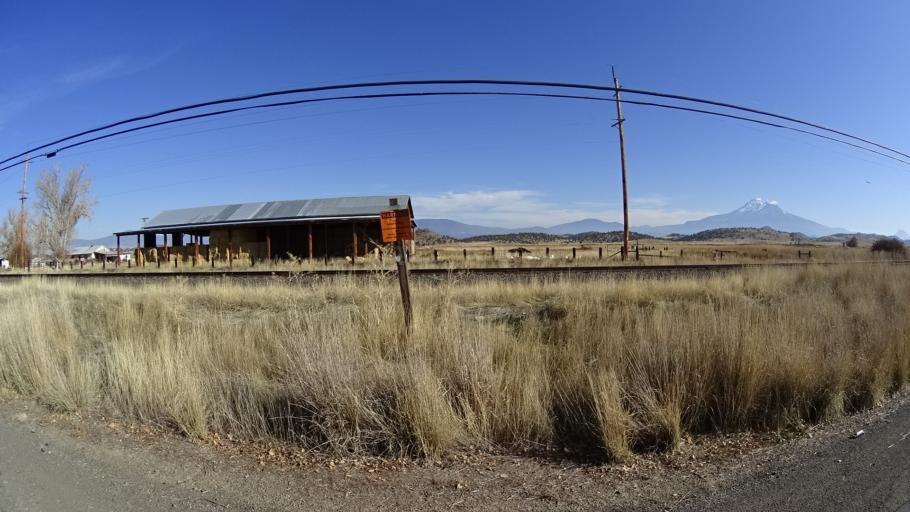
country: US
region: California
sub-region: Siskiyou County
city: Montague
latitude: 41.6352
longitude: -122.5218
